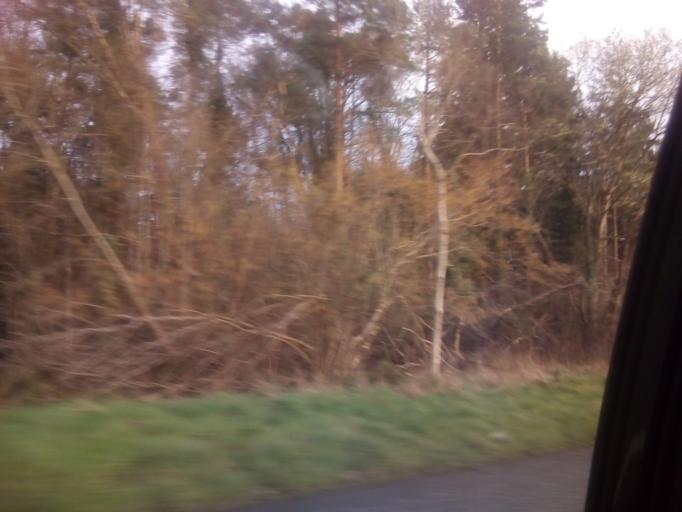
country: IE
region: Leinster
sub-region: Laois
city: Abbeyleix
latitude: 52.9026
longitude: -7.3559
